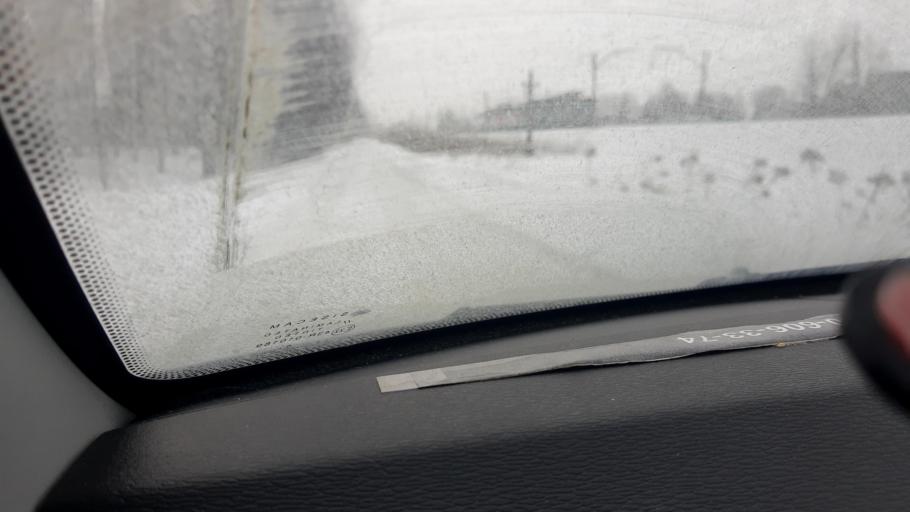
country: RU
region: Nizjnij Novgorod
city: Sitniki
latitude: 56.5264
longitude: 44.0536
